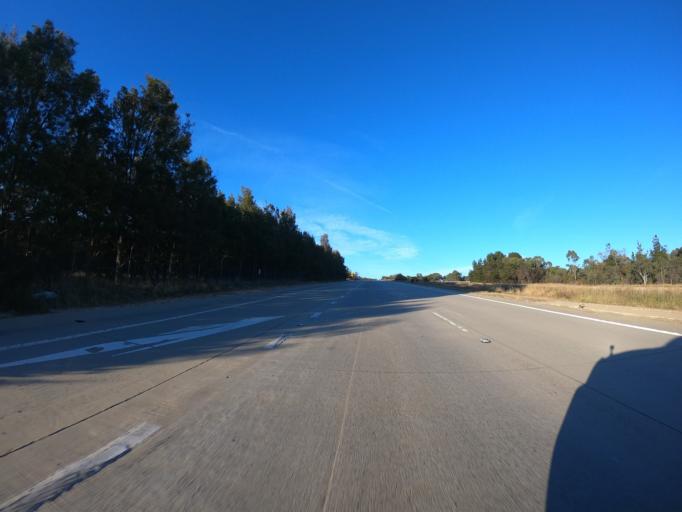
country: AU
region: New South Wales
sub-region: Yass Valley
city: Gundaroo
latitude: -35.1014
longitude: 149.3744
